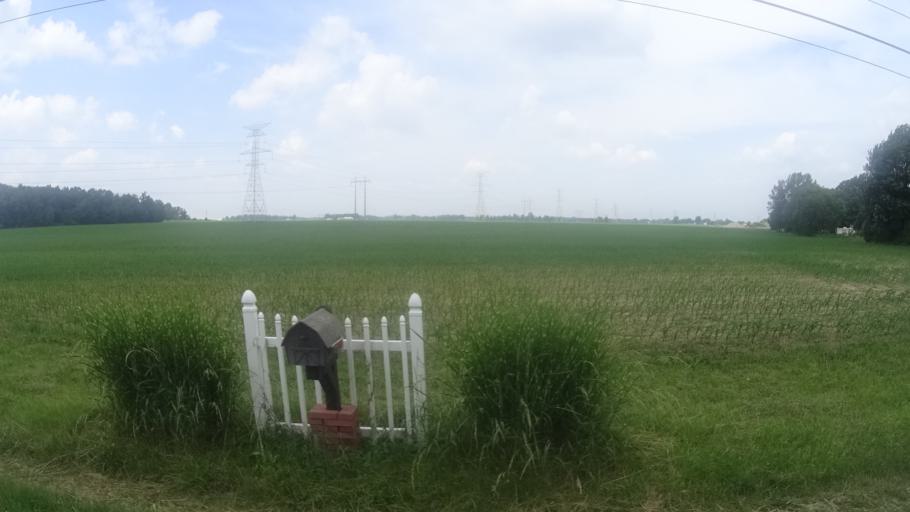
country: US
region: Ohio
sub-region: Erie County
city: Milan
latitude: 41.3471
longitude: -82.6941
